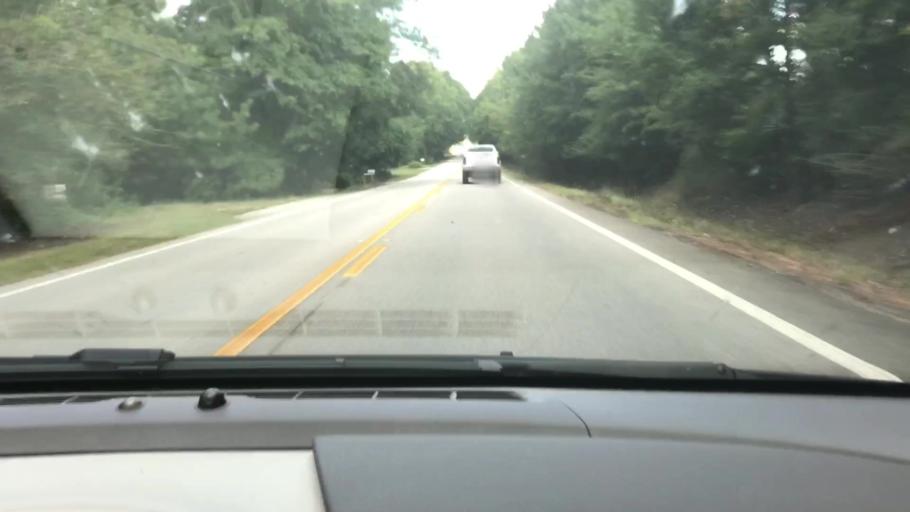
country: US
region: Georgia
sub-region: Troup County
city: La Grange
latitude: 32.9753
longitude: -85.0270
